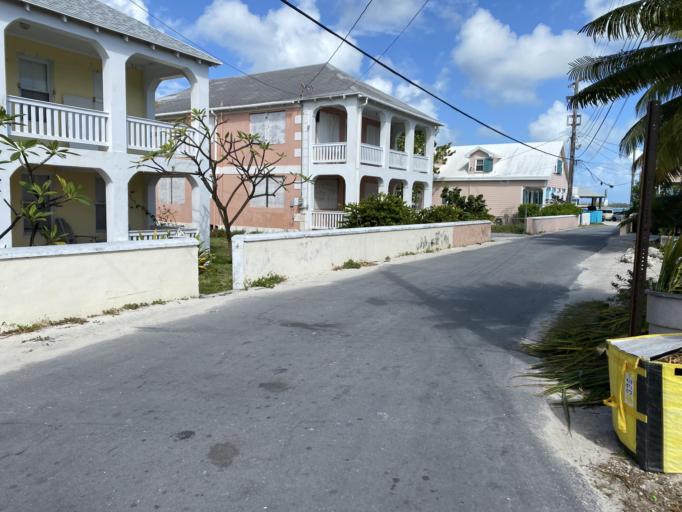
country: BS
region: Spanish Wells
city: Spanish Wells
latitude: 25.5439
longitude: -76.7450
